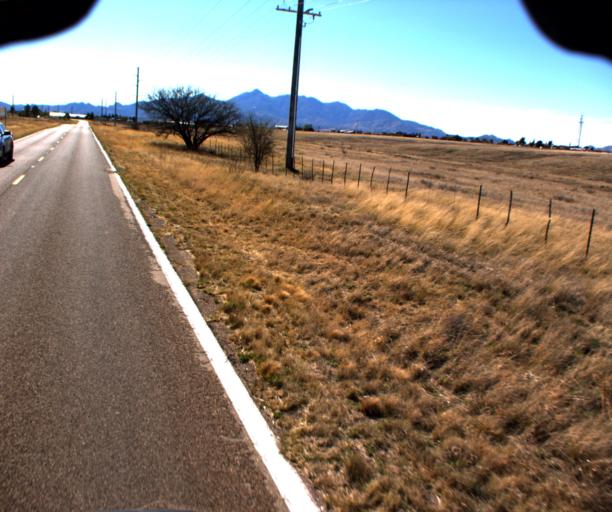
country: US
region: Arizona
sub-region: Cochise County
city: Huachuca City
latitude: 31.6752
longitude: -110.6445
